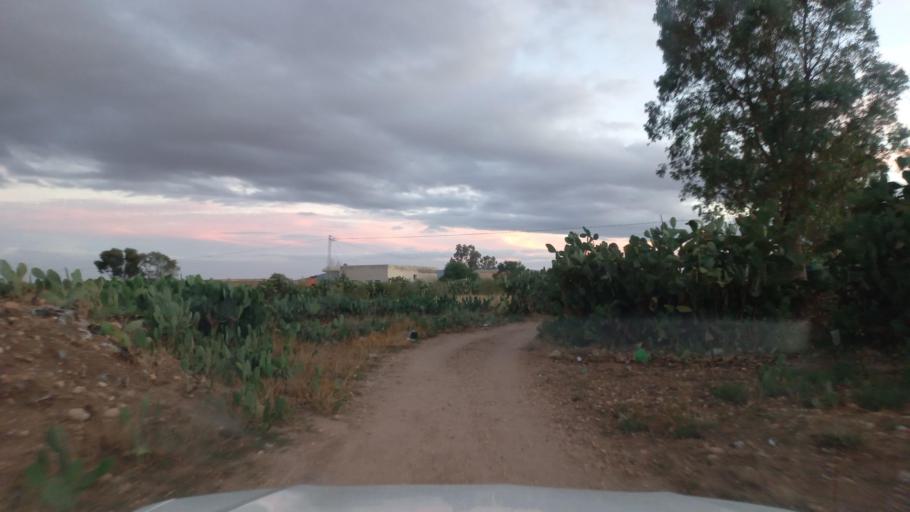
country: TN
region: Al Qasrayn
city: Kasserine
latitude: 35.2576
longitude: 8.9399
